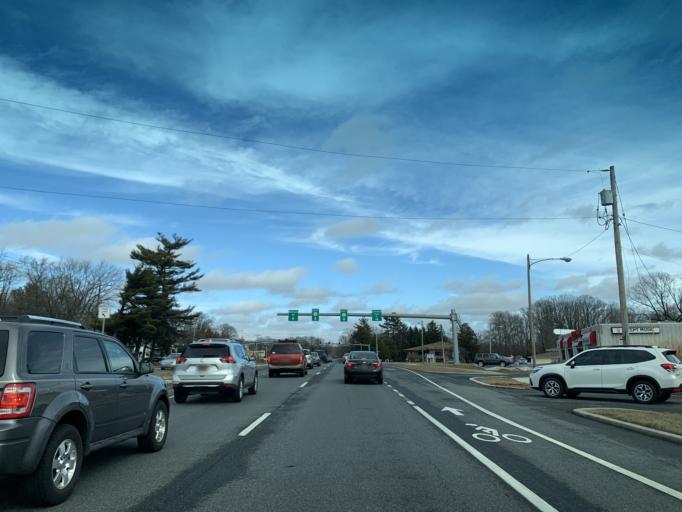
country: US
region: Delaware
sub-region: New Castle County
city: Pike Creek Valley
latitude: 39.7128
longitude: -75.6769
